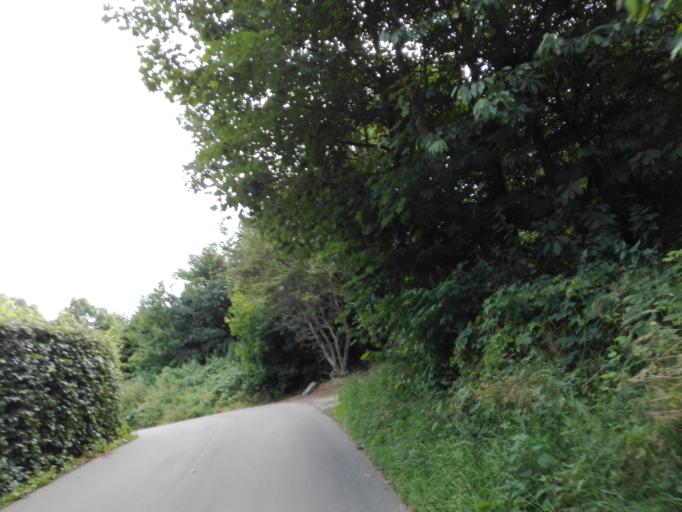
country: DK
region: Central Jutland
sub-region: Skanderborg Kommune
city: Horning
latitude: 56.0986
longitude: 10.0214
